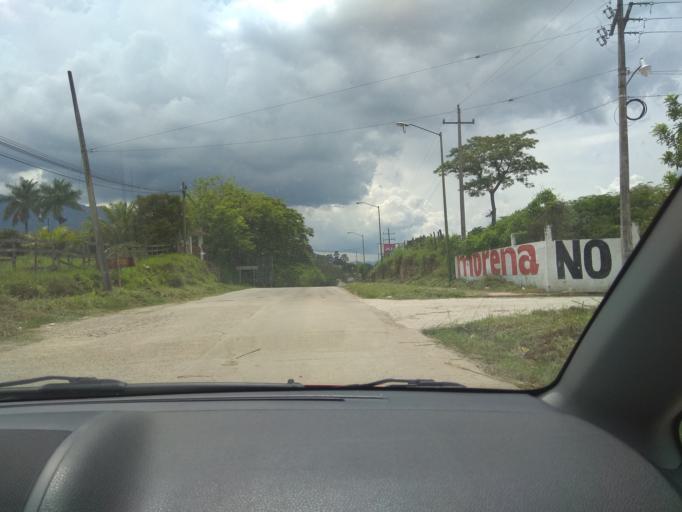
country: MX
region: Chiapas
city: Ocosingo
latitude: 16.8965
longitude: -92.0747
